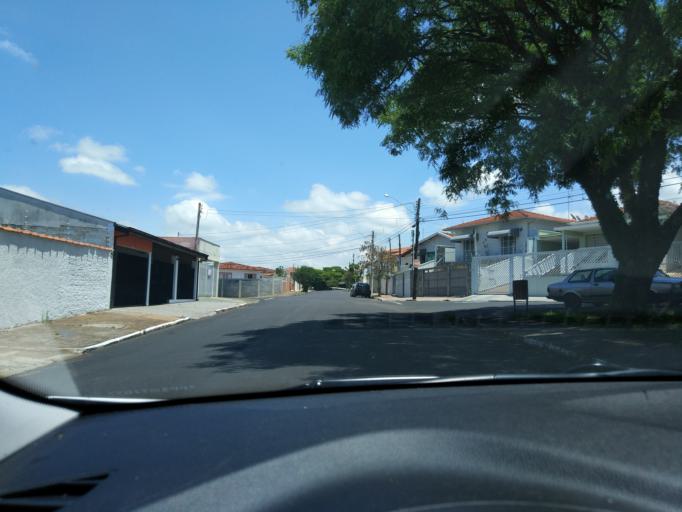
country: BR
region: Sao Paulo
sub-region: Botucatu
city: Botucatu
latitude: -22.8673
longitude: -48.4423
